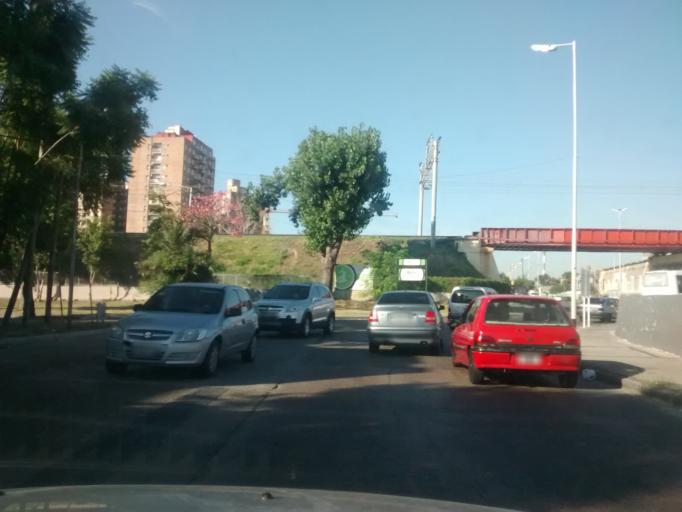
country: AR
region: Buenos Aires
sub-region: Partido de Avellaneda
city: Avellaneda
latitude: -34.6797
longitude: -58.3393
